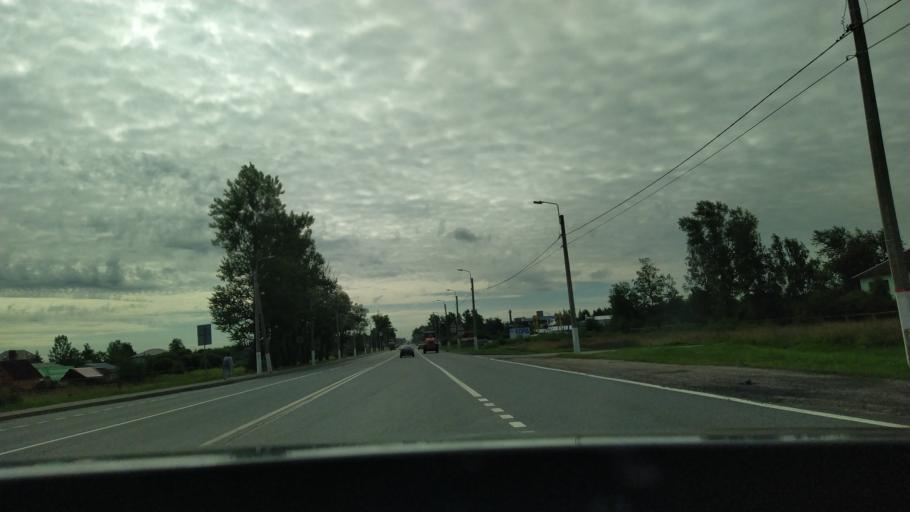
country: RU
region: Leningrad
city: Tosno
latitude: 59.5643
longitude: 30.8344
